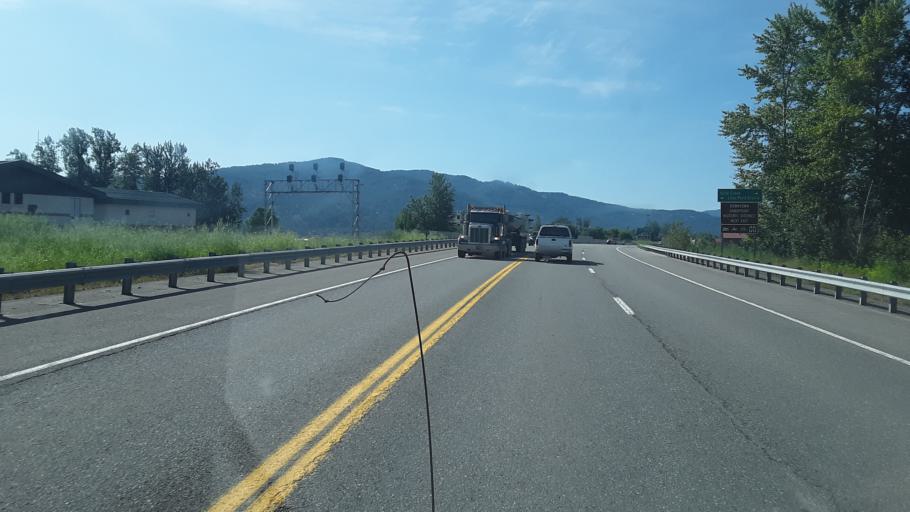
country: US
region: Idaho
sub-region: Bonner County
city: Sandpoint
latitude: 48.2812
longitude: -116.5478
